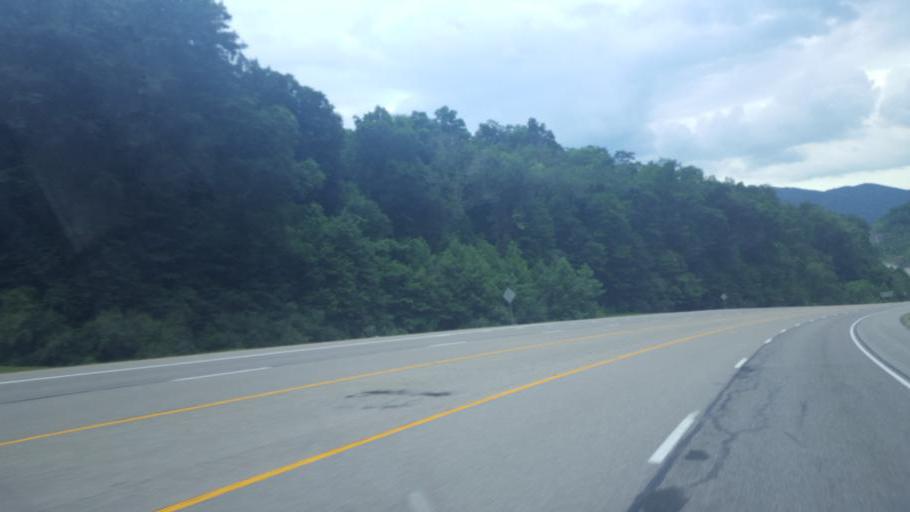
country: US
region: Kentucky
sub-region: Letcher County
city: Jenkins
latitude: 37.1820
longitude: -82.6368
